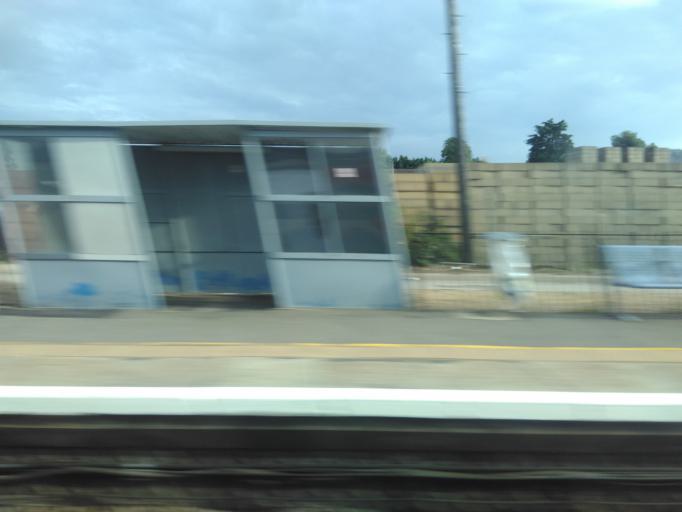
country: GB
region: England
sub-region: Norfolk
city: Weeting
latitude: 52.4538
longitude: 0.6234
